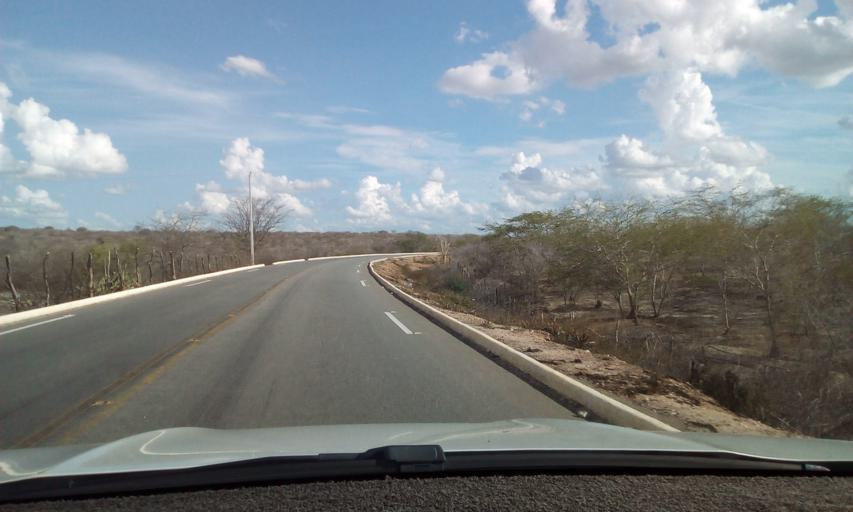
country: BR
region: Paraiba
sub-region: Soledade
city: Soledade
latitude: -6.8978
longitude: -36.3927
